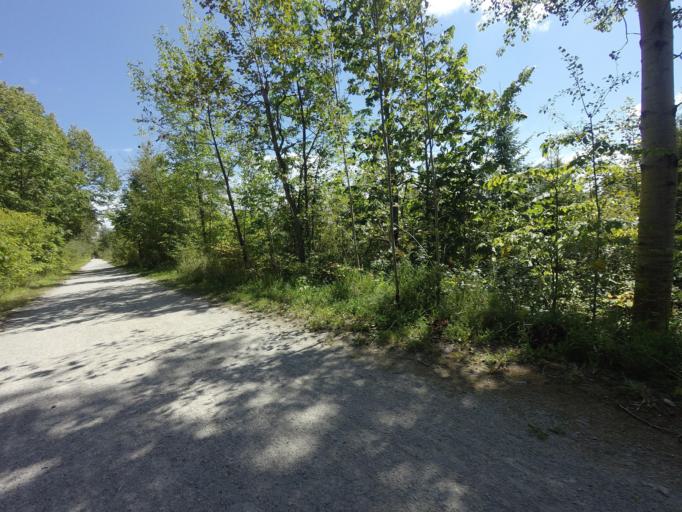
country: CA
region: Ontario
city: Orangeville
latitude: 43.7851
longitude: -80.1480
